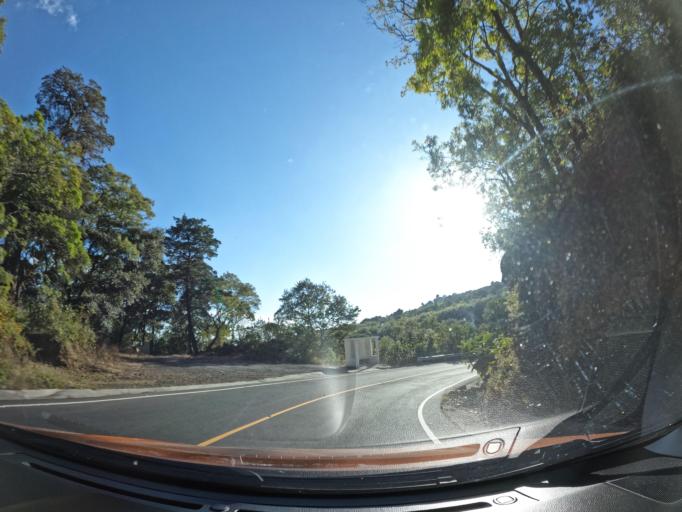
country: GT
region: Escuintla
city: Palin
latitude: 14.4584
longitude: -90.6946
